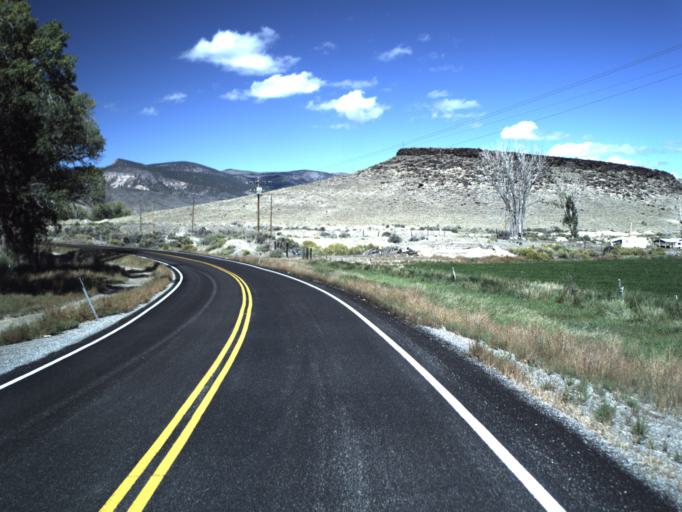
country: US
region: Utah
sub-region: Piute County
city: Junction
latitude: 38.1515
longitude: -112.0012
